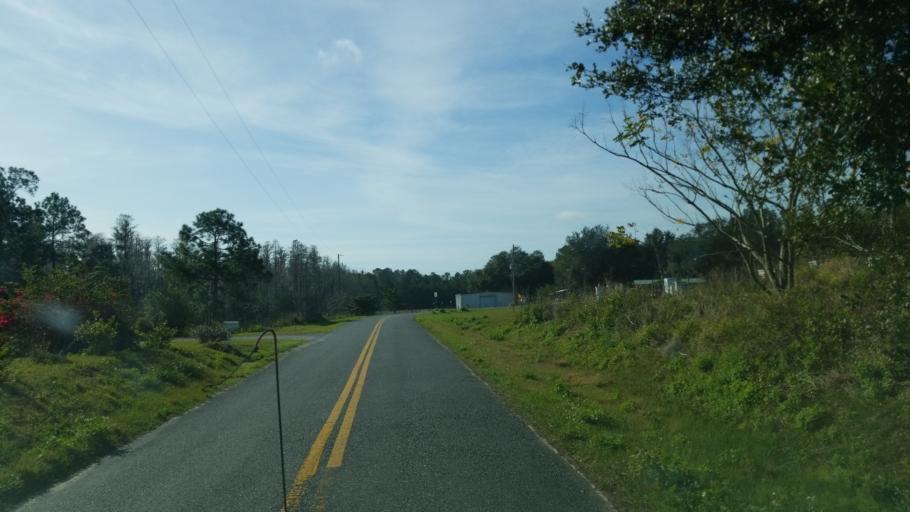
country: US
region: Florida
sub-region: Lake County
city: Clermont
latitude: 28.4460
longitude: -81.7824
